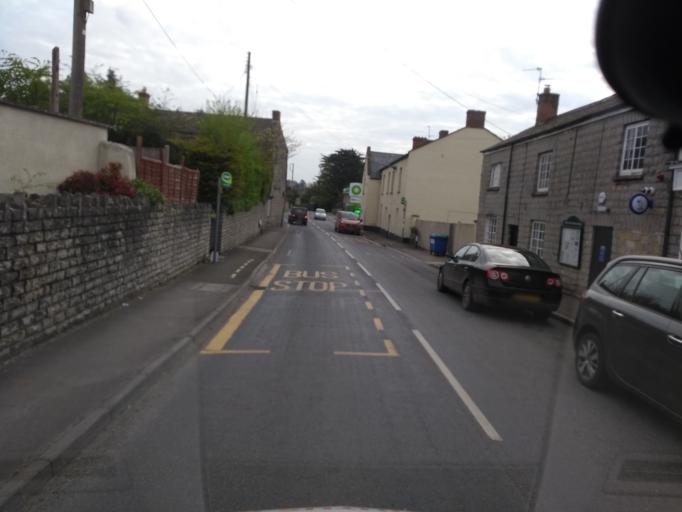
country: GB
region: England
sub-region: Somerset
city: Curry Rivel
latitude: 51.0228
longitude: -2.8692
